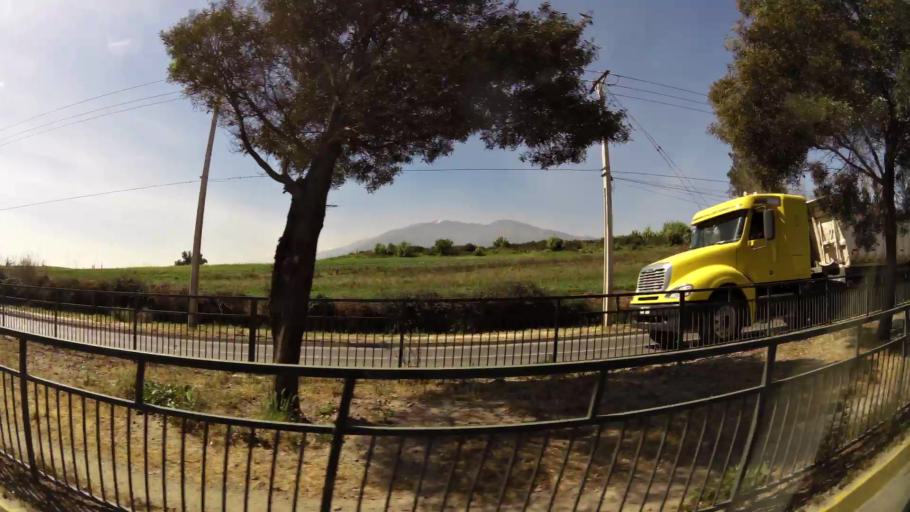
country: CL
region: Santiago Metropolitan
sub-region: Provincia de Cordillera
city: Puente Alto
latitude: -33.5853
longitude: -70.5451
